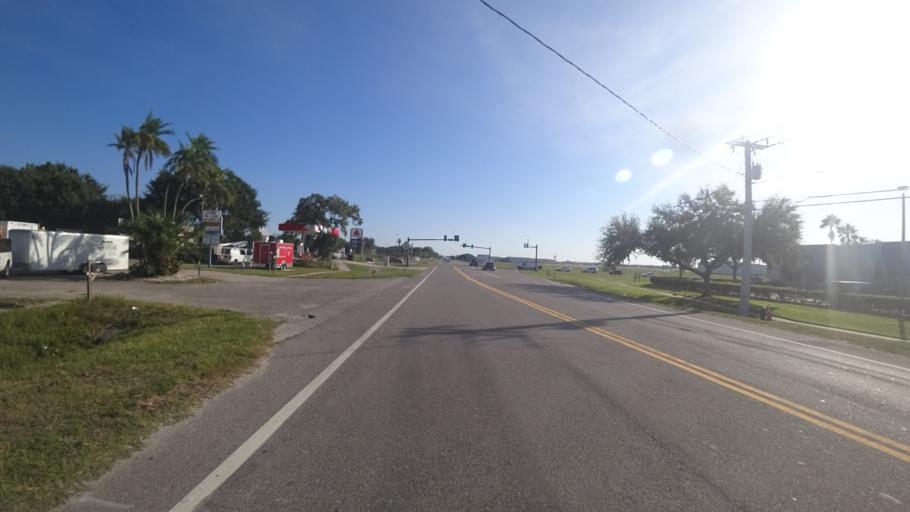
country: US
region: Florida
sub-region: Manatee County
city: Whitfield
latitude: 27.4044
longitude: -82.5468
